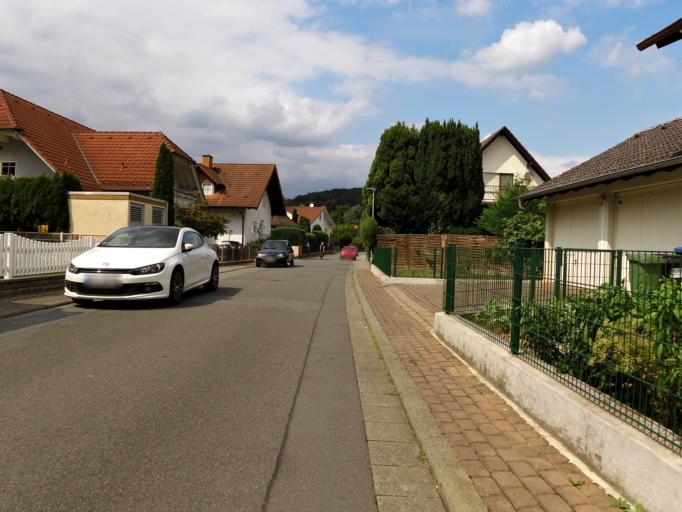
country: DE
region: Hesse
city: Hochst im Odenwald
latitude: 49.7954
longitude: 8.9978
